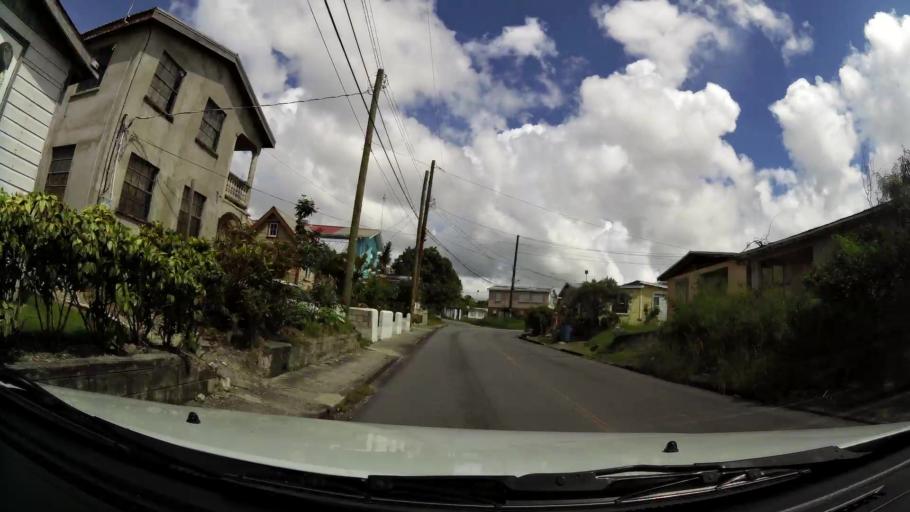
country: BB
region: Saint Michael
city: Bridgetown
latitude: 13.1347
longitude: -59.6220
